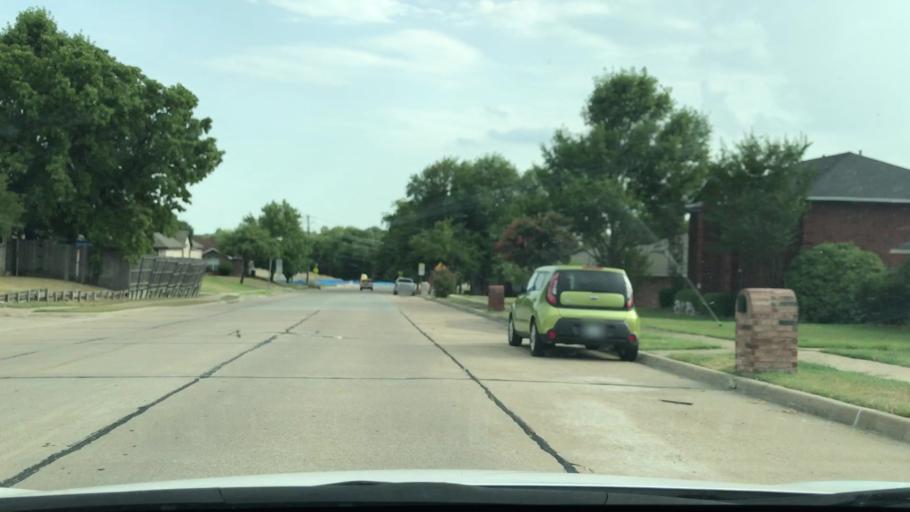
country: US
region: Texas
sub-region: Collin County
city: Wylie
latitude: 33.0127
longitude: -96.5201
